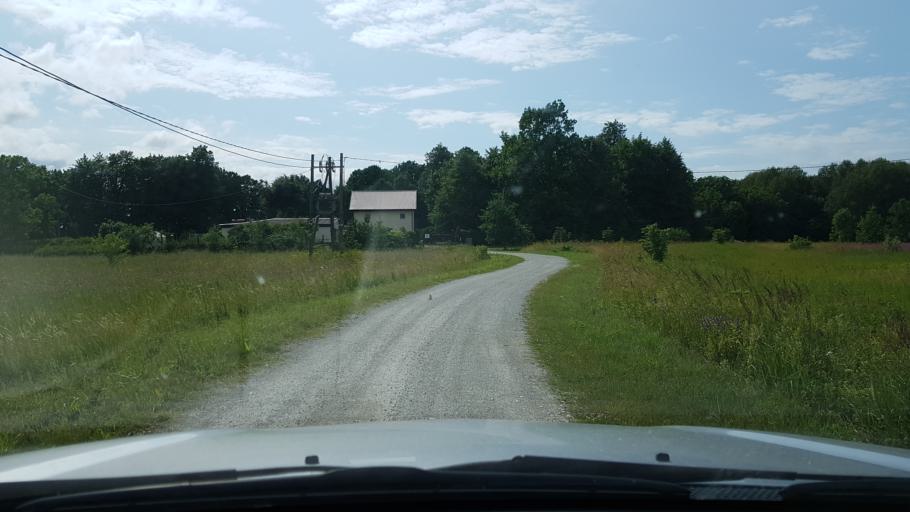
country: EE
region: Ida-Virumaa
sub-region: Narva-Joesuu linn
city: Narva-Joesuu
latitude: 59.3745
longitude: 27.9399
